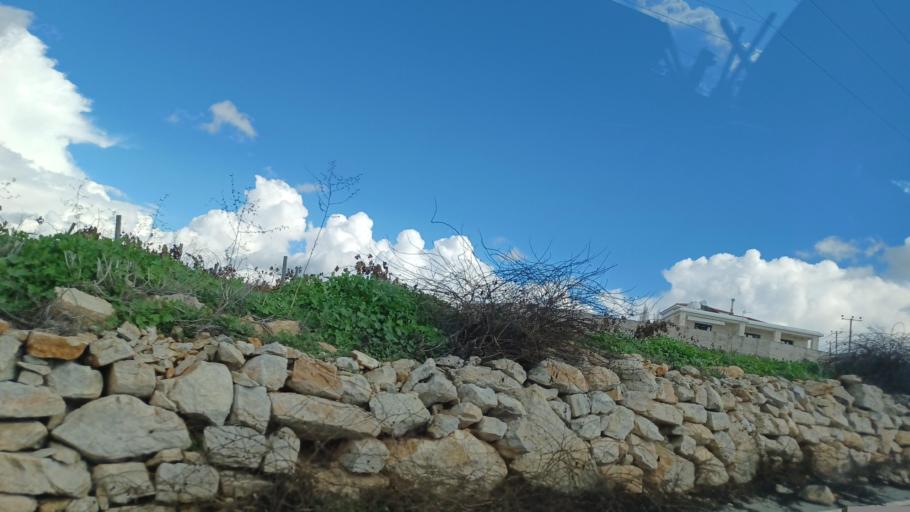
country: CY
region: Pafos
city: Pegeia
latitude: 34.9138
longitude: 32.4134
